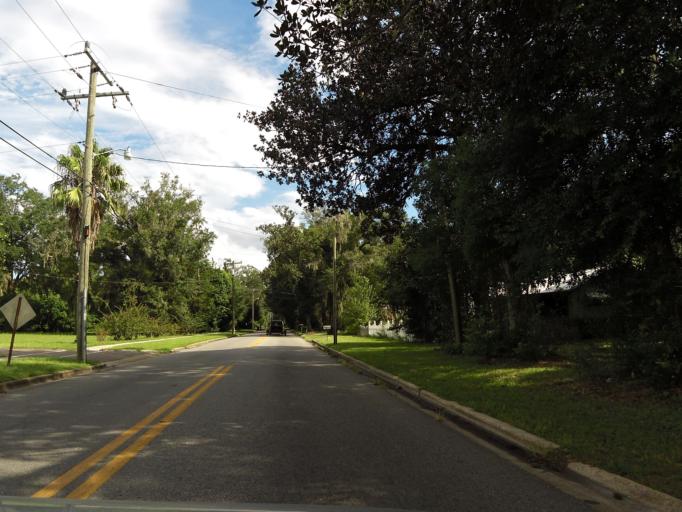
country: US
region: Florida
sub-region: Clay County
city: Green Cove Springs
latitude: 29.9846
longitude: -81.6957
